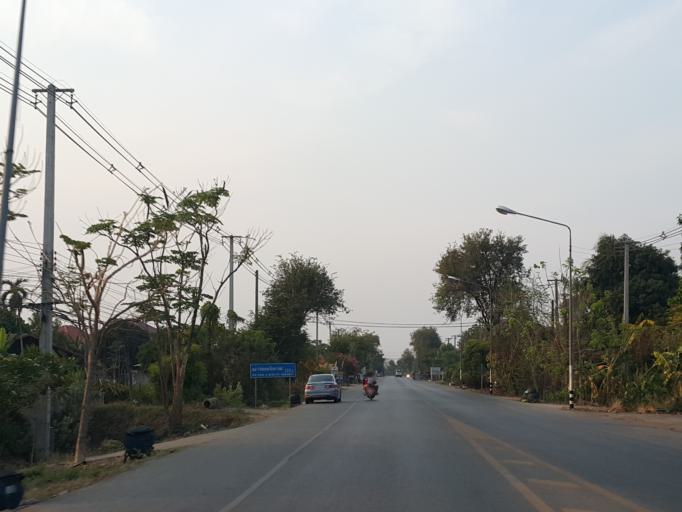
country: TH
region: Sukhothai
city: Sawankhalok
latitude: 17.2798
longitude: 99.8441
